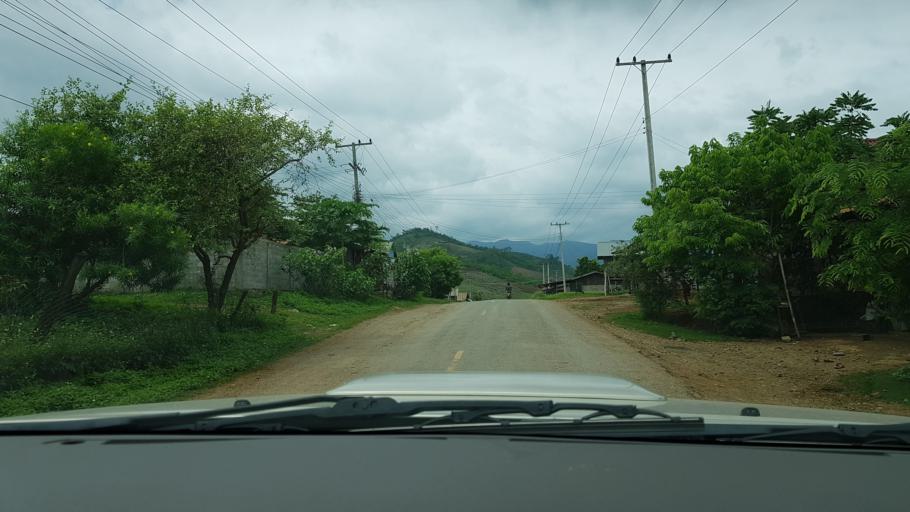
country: TH
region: Nan
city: Chaloem Phra Kiat
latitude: 19.9861
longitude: 101.2763
